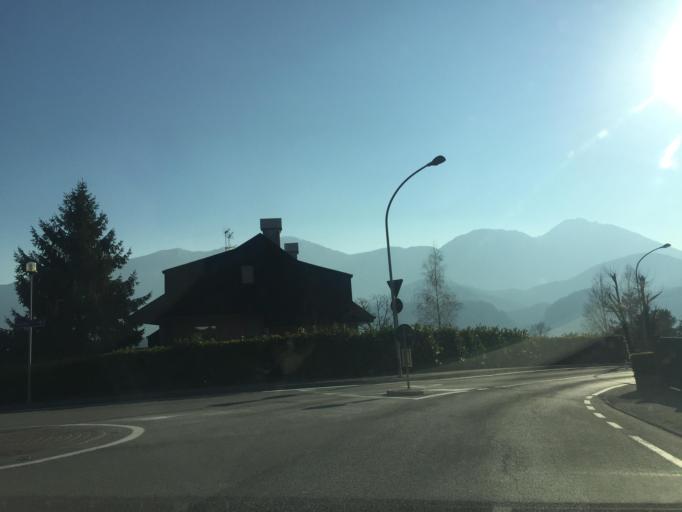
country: IT
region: Friuli Venezia Giulia
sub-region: Provincia di Udine
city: Tolmezzo
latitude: 46.3992
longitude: 13.0359
